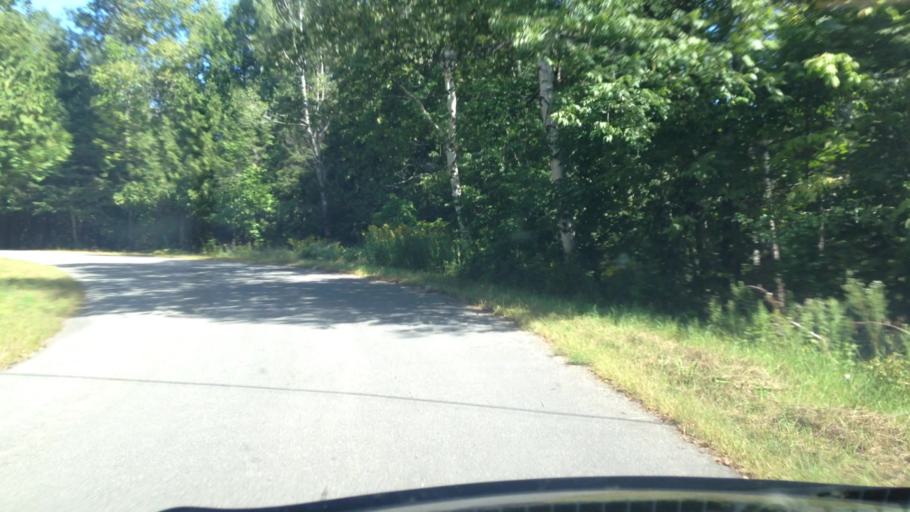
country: CA
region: Quebec
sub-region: Laurentides
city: Mont-Tremblant
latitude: 45.9415
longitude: -74.5872
